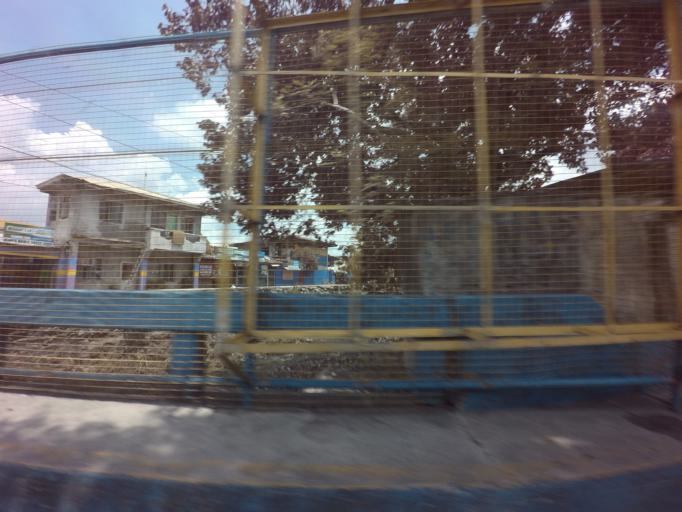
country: PH
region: Calabarzon
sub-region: Province of Laguna
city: San Pedro
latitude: 14.3865
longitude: 121.0501
